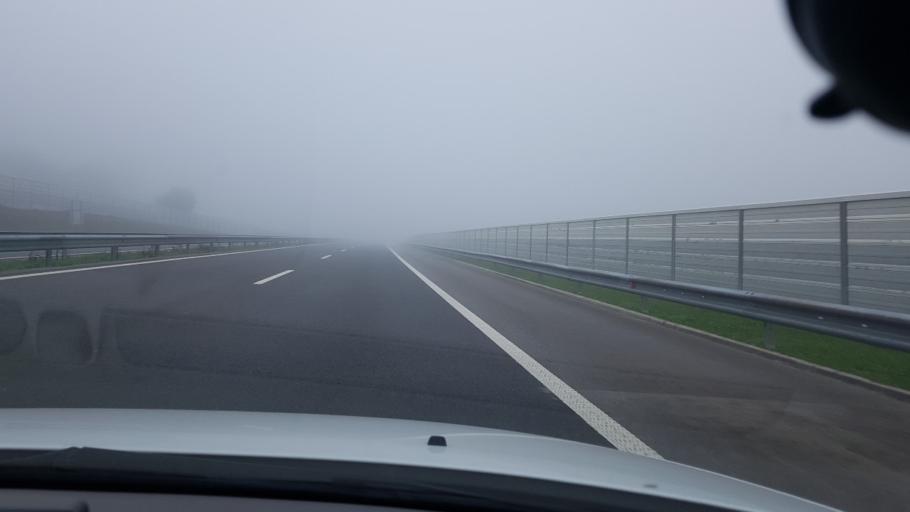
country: SI
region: Kostanjevica na Krki
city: Kostanjevica na Krki
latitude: 45.9072
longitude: 15.3792
